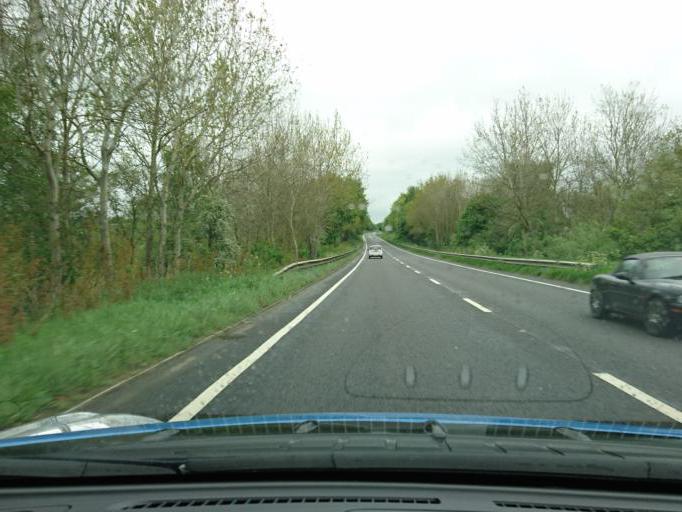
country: GB
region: England
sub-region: Oxfordshire
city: Shrivenham
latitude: 51.6096
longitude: -1.6566
